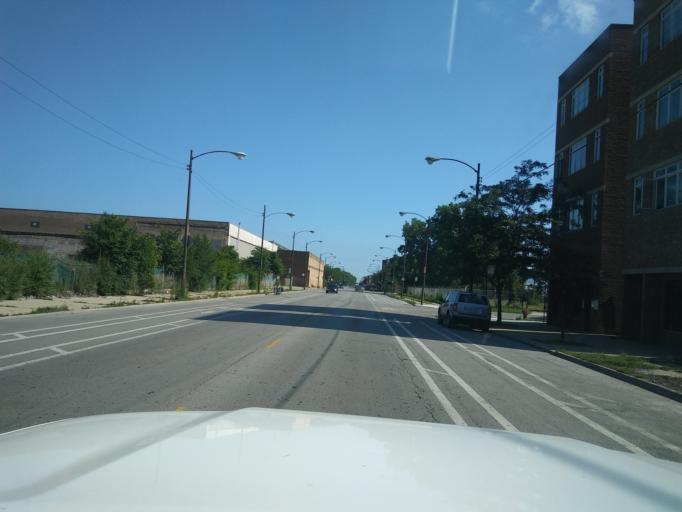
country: US
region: Illinois
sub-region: Cook County
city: Chicago
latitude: 41.8057
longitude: -87.6455
